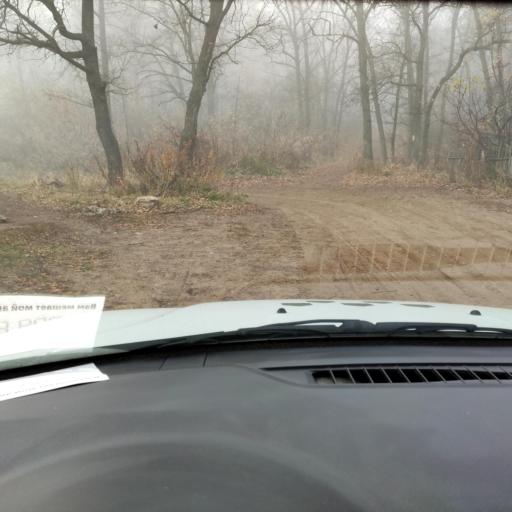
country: RU
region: Samara
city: Tol'yatti
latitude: 53.5311
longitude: 49.3883
